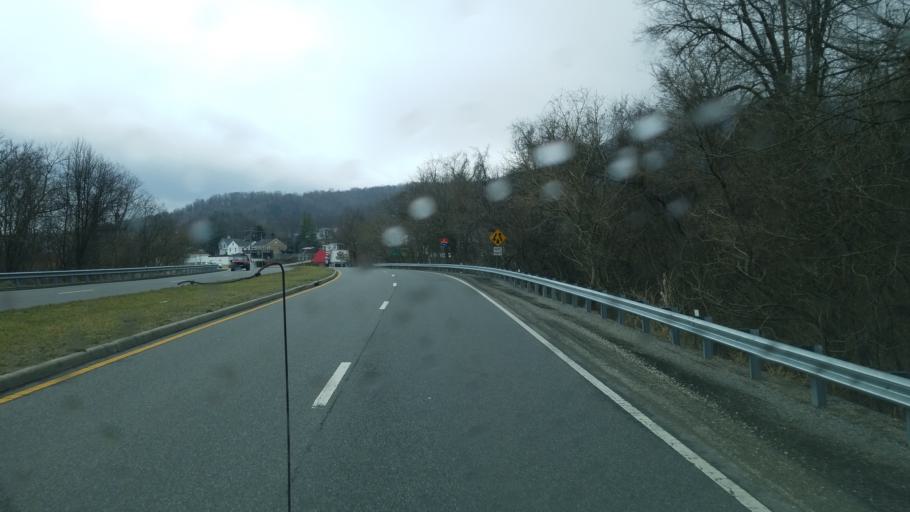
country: US
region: Virginia
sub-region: Giles County
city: Pearisburg
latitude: 37.3325
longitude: -80.7383
